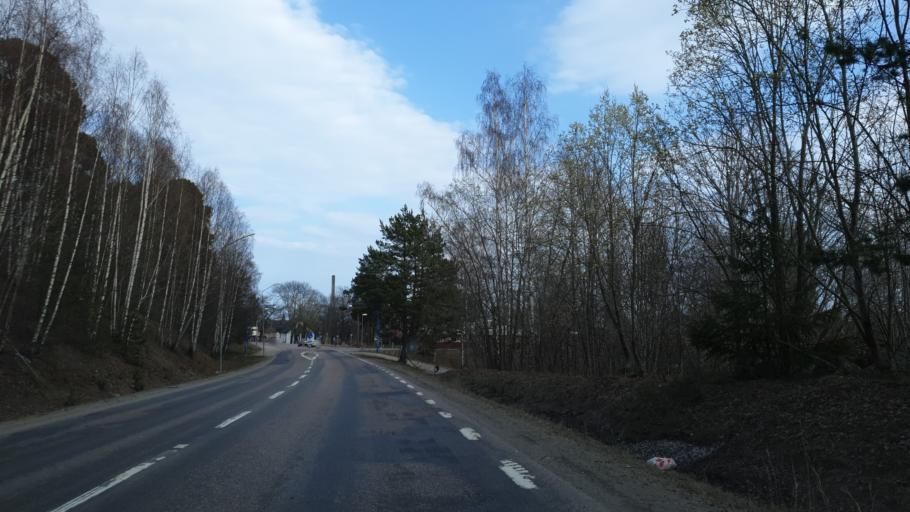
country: SE
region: Gaevleborg
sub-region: Hudiksvalls Kommun
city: Iggesund
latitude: 61.6410
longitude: 17.0712
